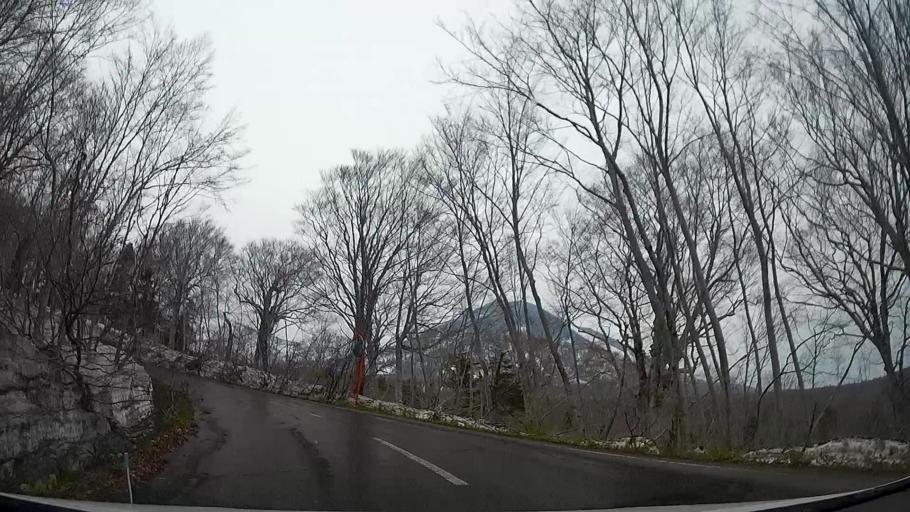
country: JP
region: Aomori
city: Aomori Shi
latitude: 40.6315
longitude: 140.9074
